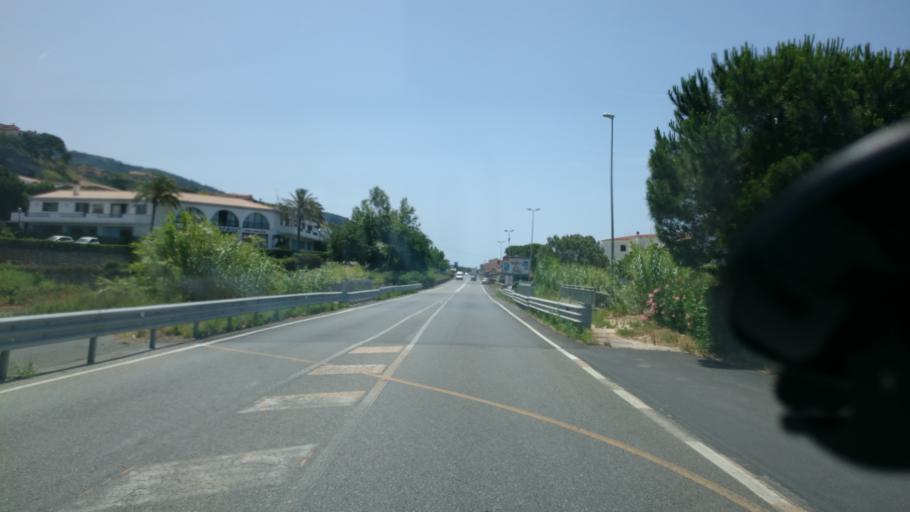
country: IT
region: Calabria
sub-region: Provincia di Cosenza
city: Cittadella del Capo
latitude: 39.5730
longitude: 15.8717
